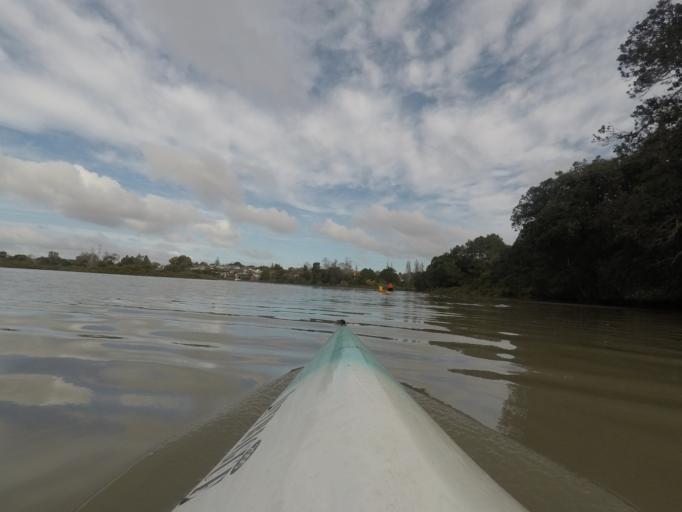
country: NZ
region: Auckland
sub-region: Auckland
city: Rosebank
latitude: -36.8965
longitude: 174.6725
